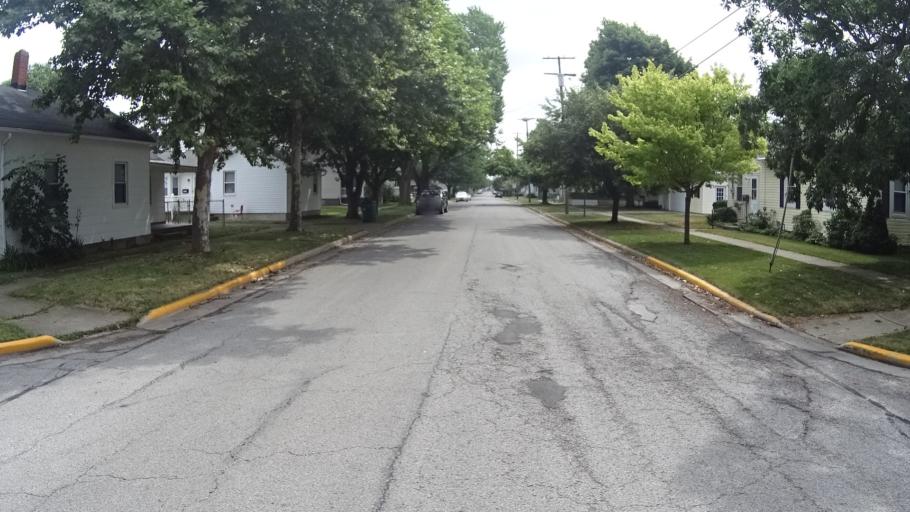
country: US
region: Ohio
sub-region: Erie County
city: Sandusky
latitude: 41.4452
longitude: -82.7261
